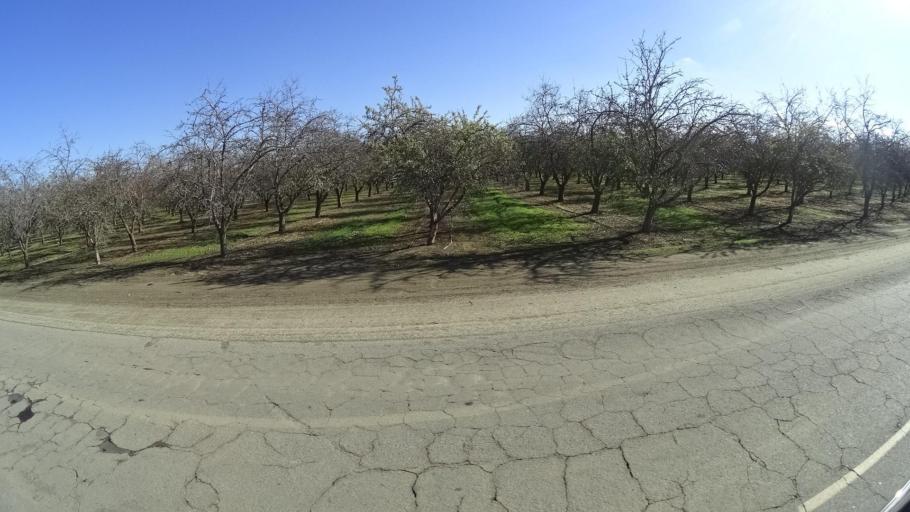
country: US
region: California
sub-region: Kern County
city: McFarland
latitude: 35.7150
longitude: -119.2586
